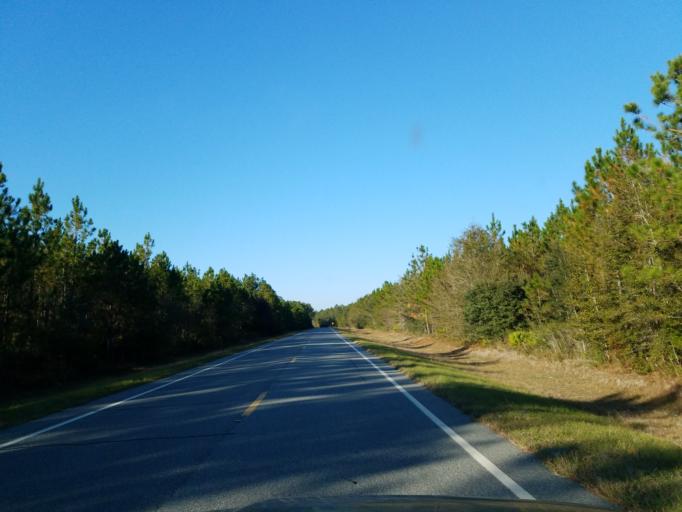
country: US
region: Georgia
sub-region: Echols County
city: Statenville
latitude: 30.8556
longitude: -83.0522
